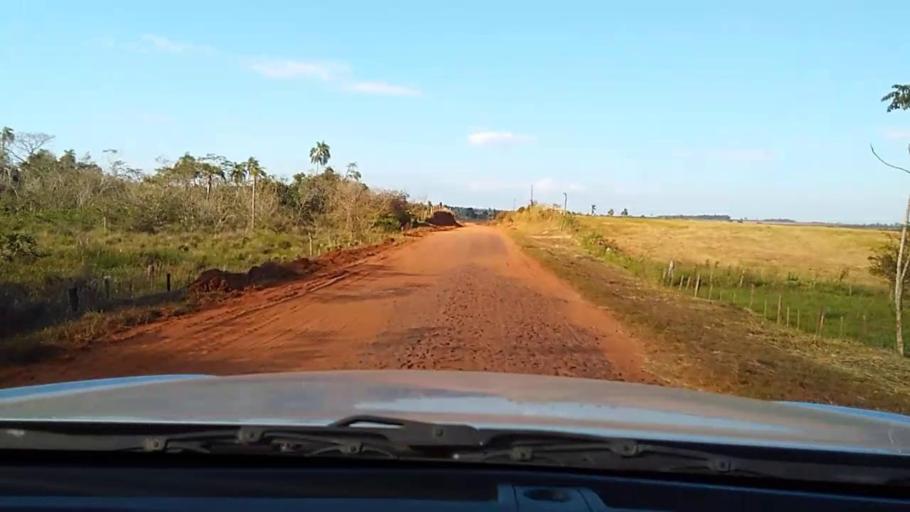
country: PY
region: Alto Parana
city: Doctor Juan Leon Mallorquin
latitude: -25.6998
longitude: -55.3812
